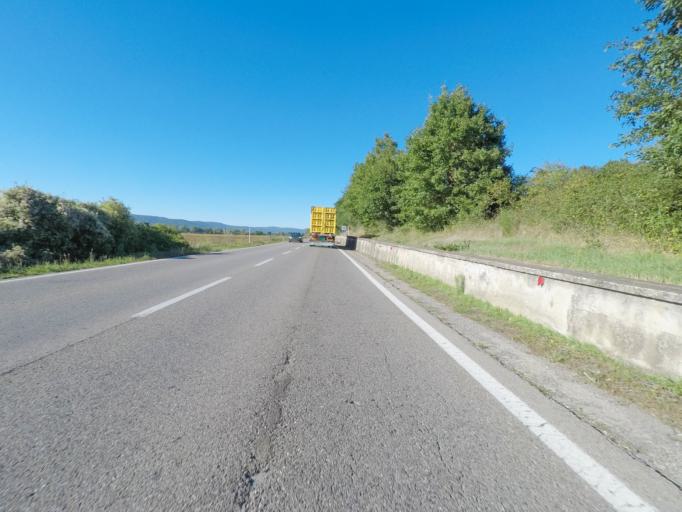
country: IT
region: Tuscany
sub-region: Provincia di Siena
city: Rosia
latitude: 43.2143
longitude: 11.2771
